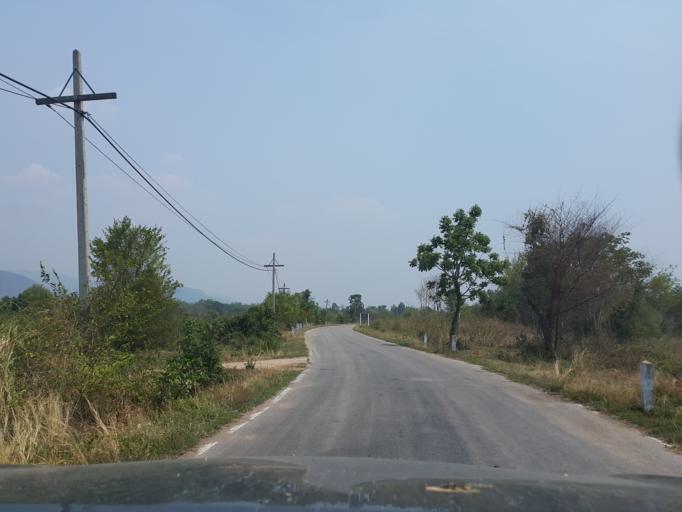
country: TH
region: Lampang
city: Mae Phrik
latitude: 17.5236
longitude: 99.1477
